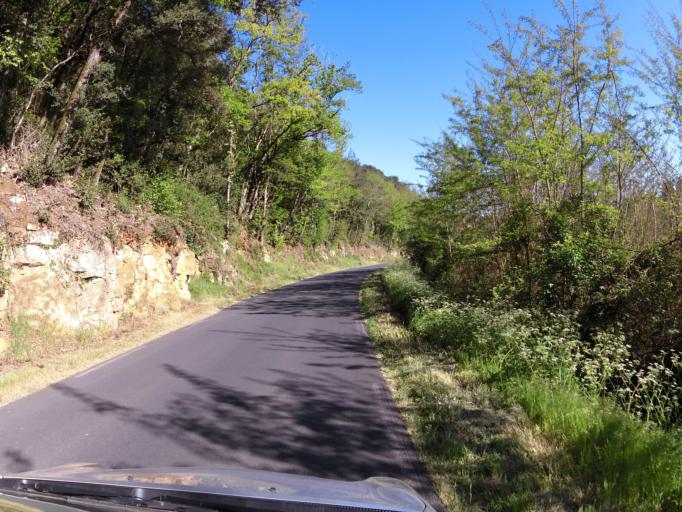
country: FR
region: Aquitaine
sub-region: Departement de la Dordogne
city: Carsac-Aillac
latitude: 44.8422
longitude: 1.2683
